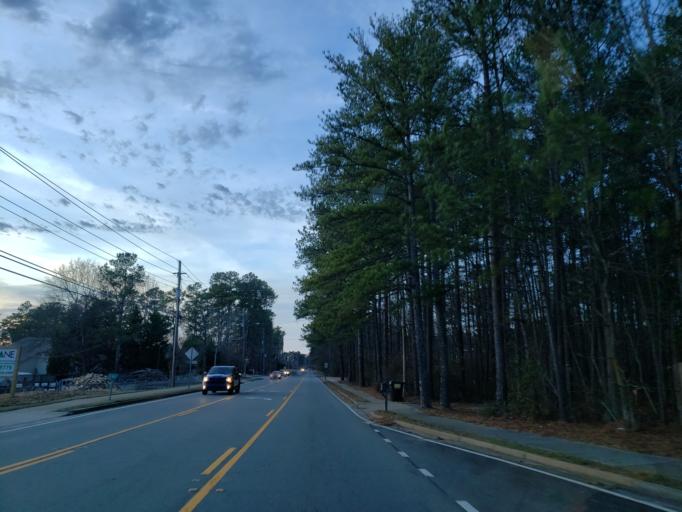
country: US
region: Georgia
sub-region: Cobb County
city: Kennesaw
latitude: 34.0668
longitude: -84.6269
